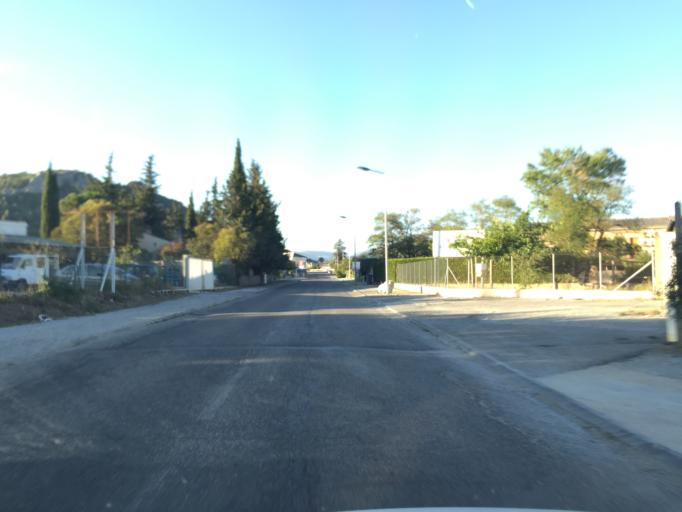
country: FR
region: Provence-Alpes-Cote d'Azur
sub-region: Departement des Alpes-de-Haute-Provence
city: Volonne
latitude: 44.0785
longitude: 6.0026
